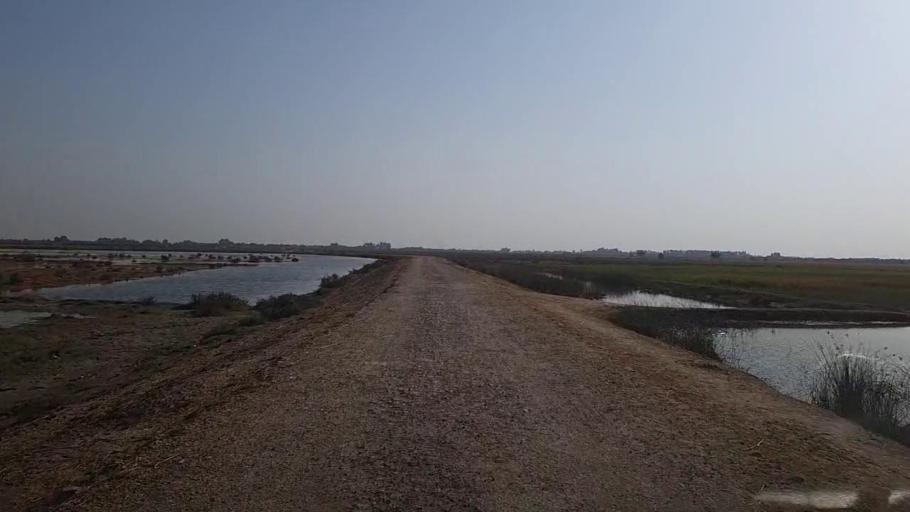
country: PK
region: Sindh
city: Kandhkot
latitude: 28.3666
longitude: 69.3298
